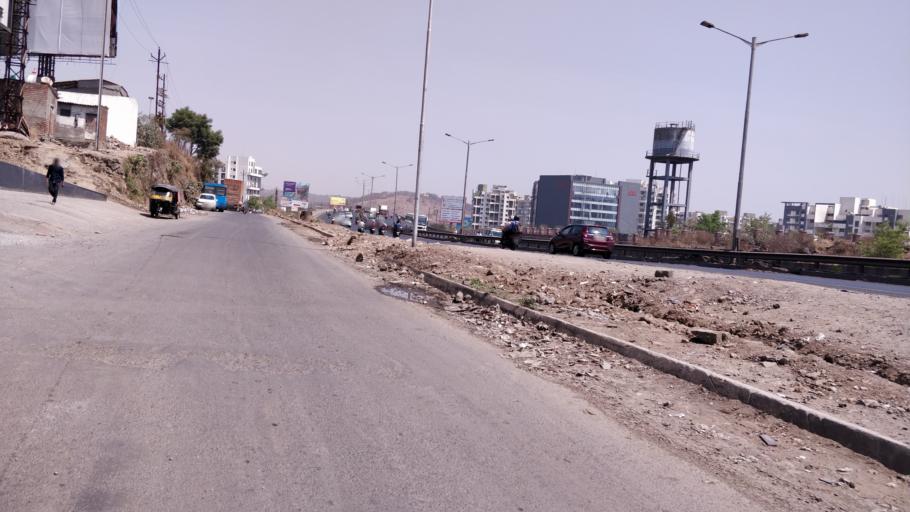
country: IN
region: Maharashtra
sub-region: Pune Division
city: Kharakvasla
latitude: 18.5167
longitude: 73.7687
